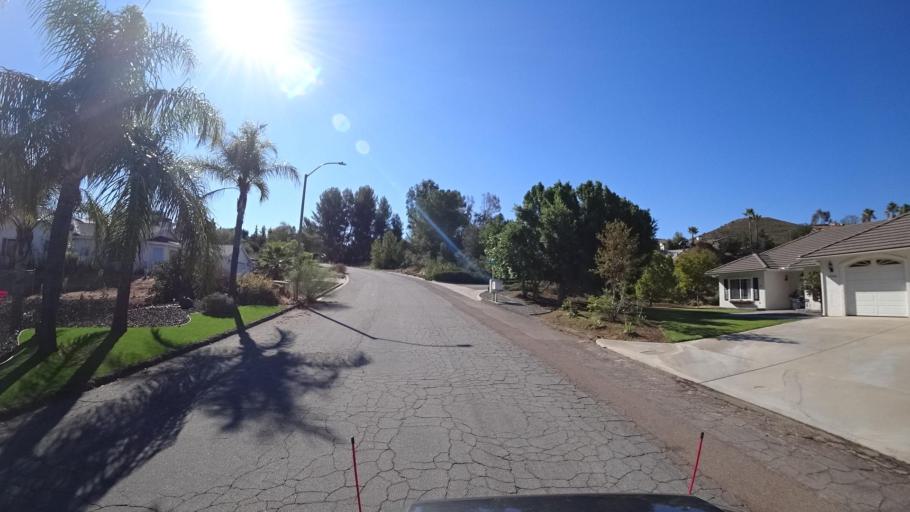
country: US
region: California
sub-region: San Diego County
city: San Diego Country Estates
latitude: 32.9986
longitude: -116.7572
